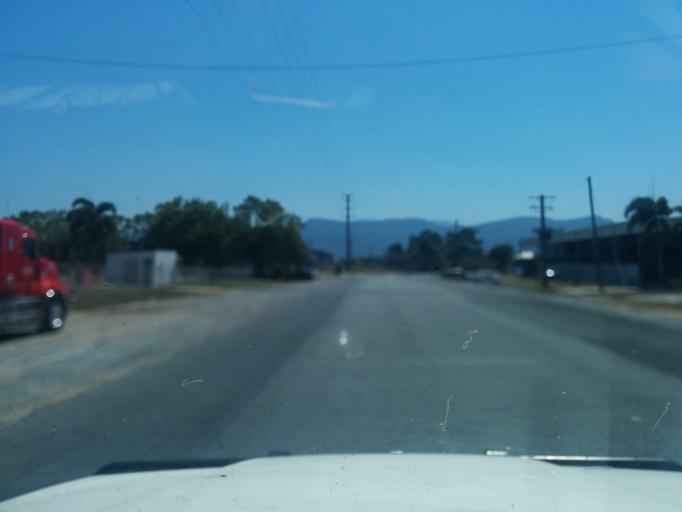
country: AU
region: Queensland
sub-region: Cairns
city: Cairns
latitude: -16.9301
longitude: 145.7735
